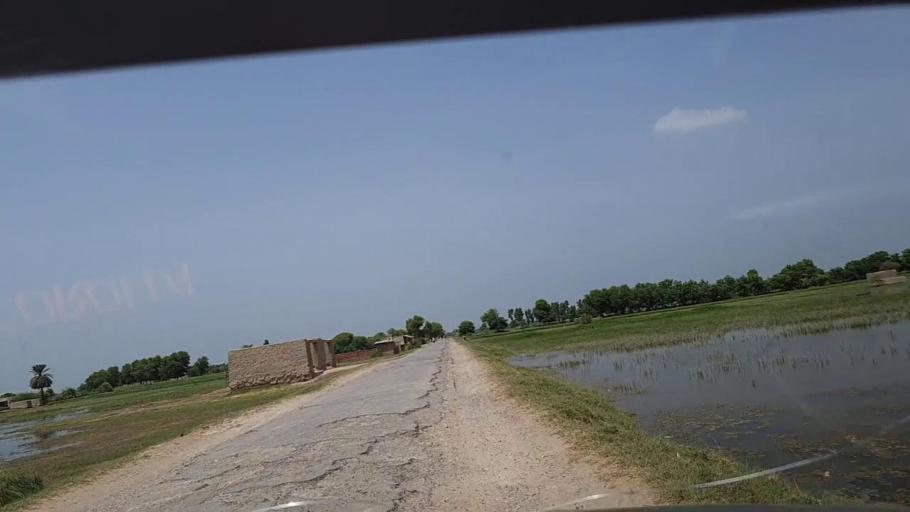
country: PK
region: Sindh
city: Khanpur
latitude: 27.8245
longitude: 69.4434
